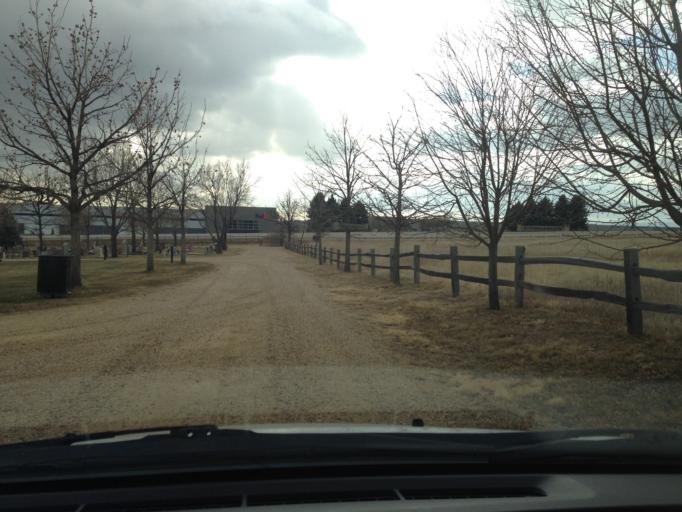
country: US
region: Colorado
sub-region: Boulder County
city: Louisville
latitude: 39.9735
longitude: -105.1121
